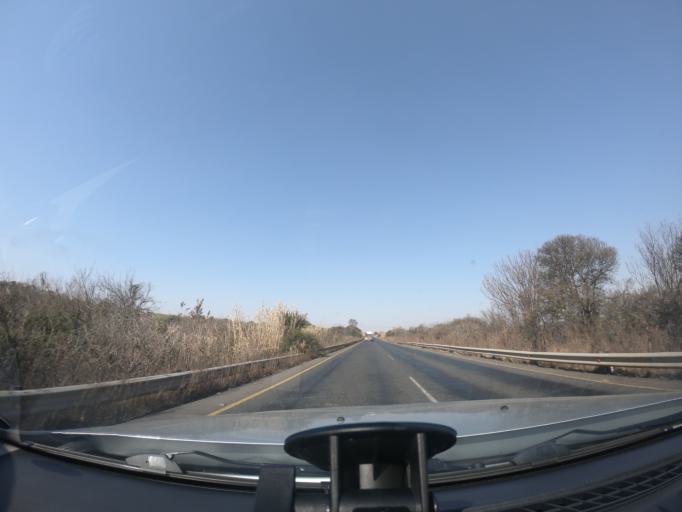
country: ZA
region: KwaZulu-Natal
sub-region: uThukela District Municipality
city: Ladysmith
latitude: -28.7431
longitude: 29.8196
